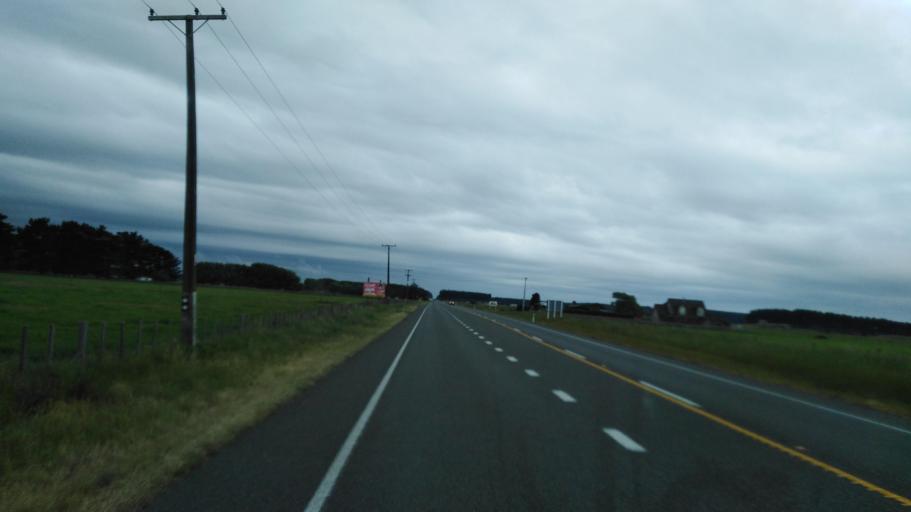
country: NZ
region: Manawatu-Wanganui
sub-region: Horowhenua District
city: Foxton
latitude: -40.3955
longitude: 175.3137
